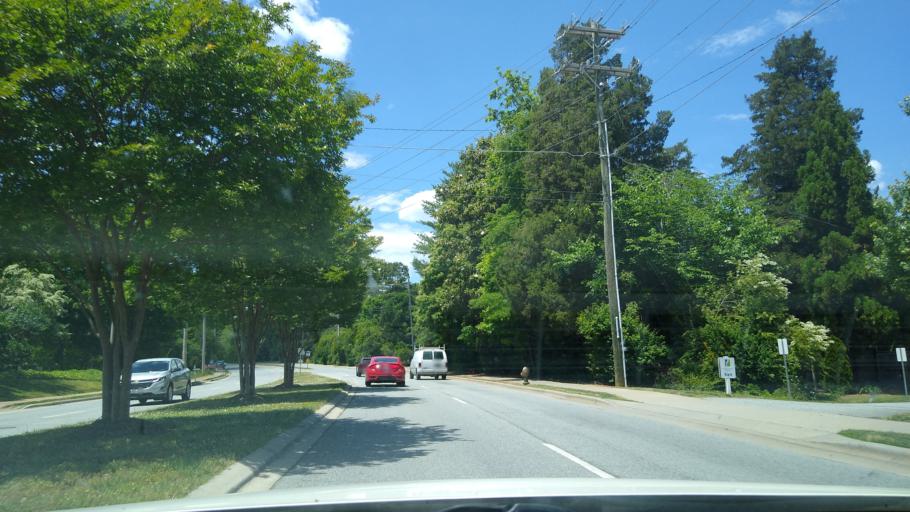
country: US
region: North Carolina
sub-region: Guilford County
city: Greensboro
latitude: 36.0899
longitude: -79.8518
